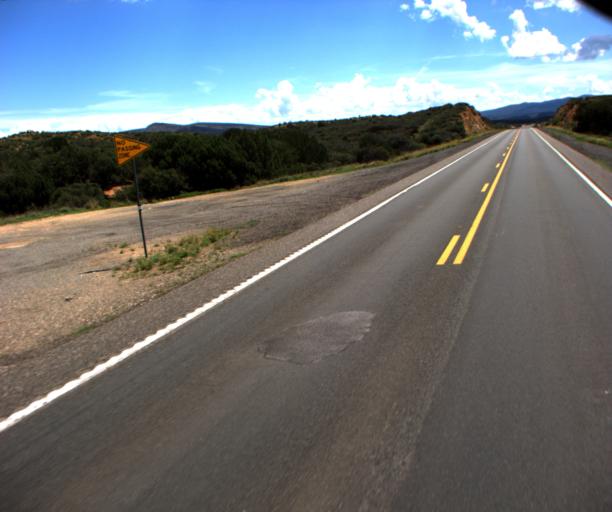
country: US
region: Arizona
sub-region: Yavapai County
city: Dewey-Humboldt
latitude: 34.5276
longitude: -112.0971
